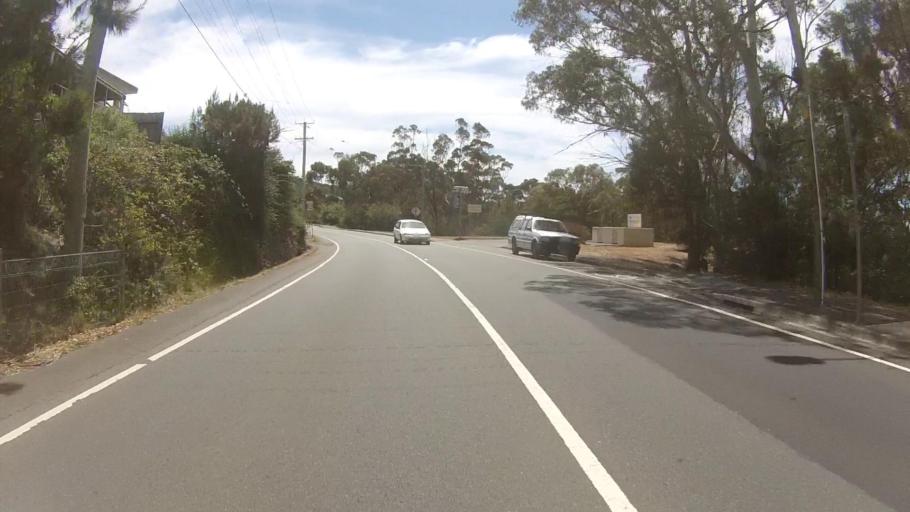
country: AU
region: Tasmania
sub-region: Kingborough
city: Taroona
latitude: -42.9424
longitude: 147.3525
